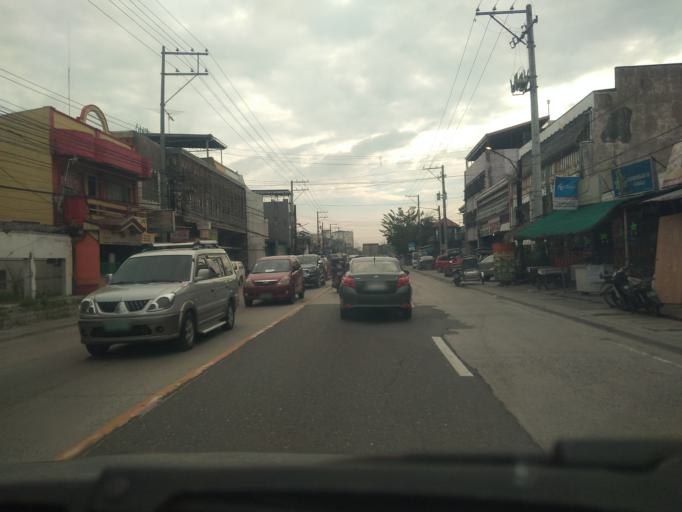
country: PH
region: Central Luzon
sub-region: Province of Pampanga
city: San Fernando
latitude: 15.0333
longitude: 120.6890
